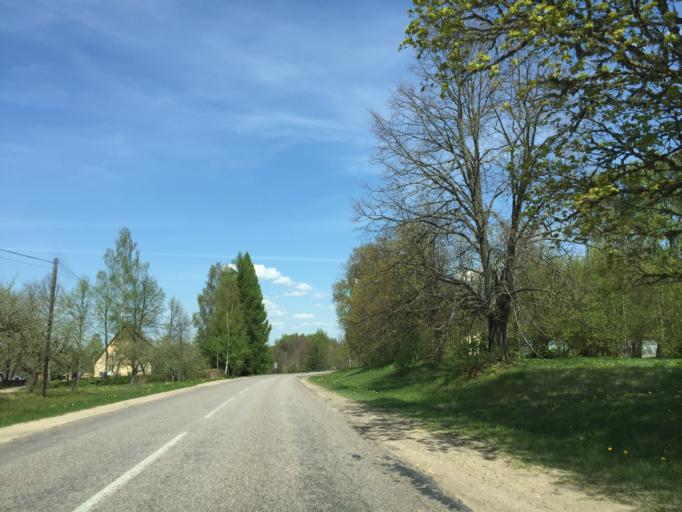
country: LV
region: Krimulda
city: Ragana
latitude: 57.3235
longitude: 24.6404
